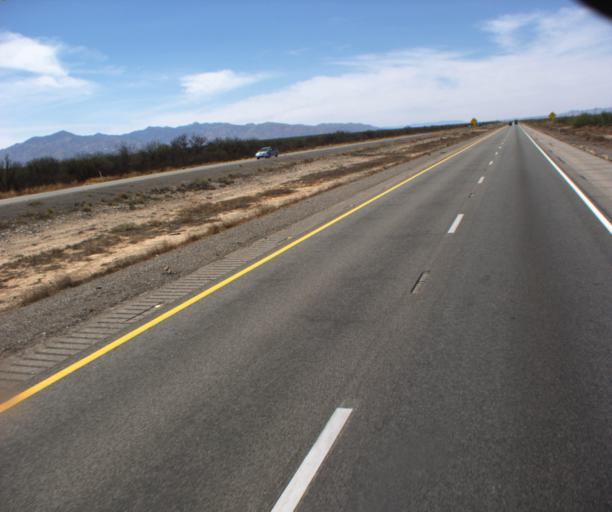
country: US
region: Arizona
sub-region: Cochise County
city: Willcox
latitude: 32.2866
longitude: -109.3065
